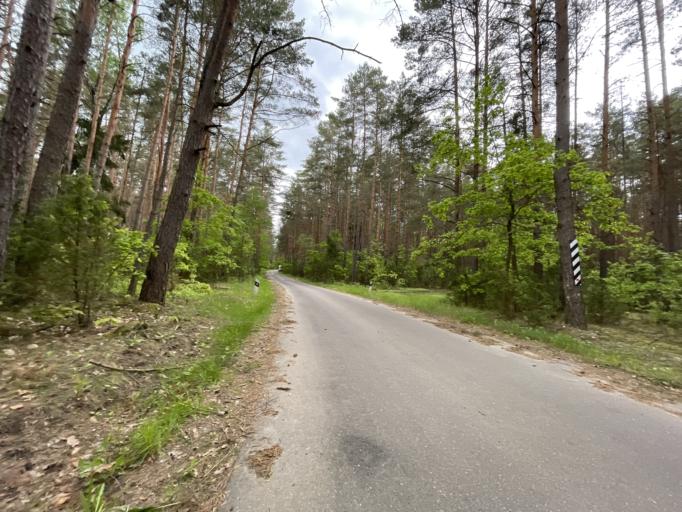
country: BY
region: Minsk
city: Stowbtsy
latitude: 53.4276
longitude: 26.8118
